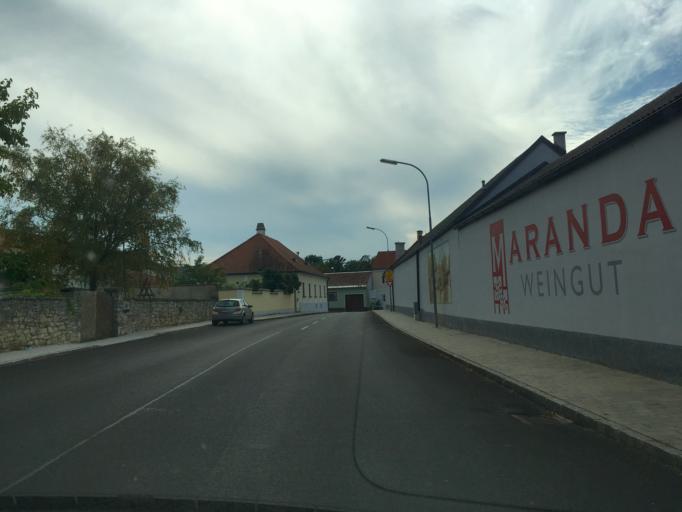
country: AT
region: Lower Austria
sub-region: Politischer Bezirk Bruck an der Leitha
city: Trautmannsdorf an der Leitha
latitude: 48.0214
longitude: 16.6776
